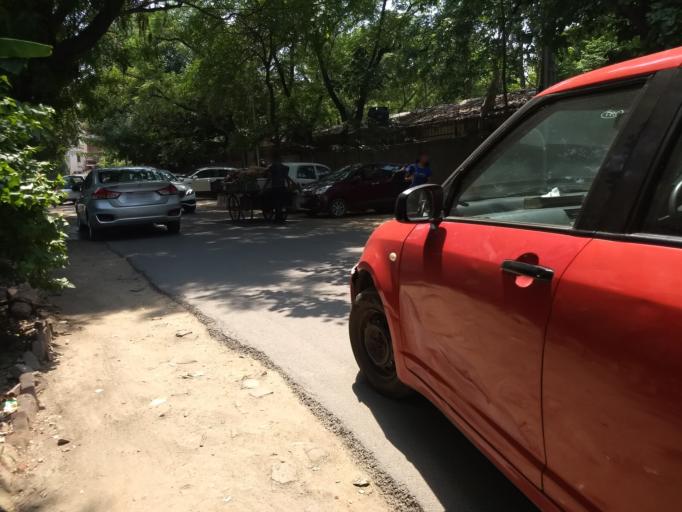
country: IN
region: NCT
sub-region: New Delhi
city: New Delhi
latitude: 28.5594
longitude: 77.2146
